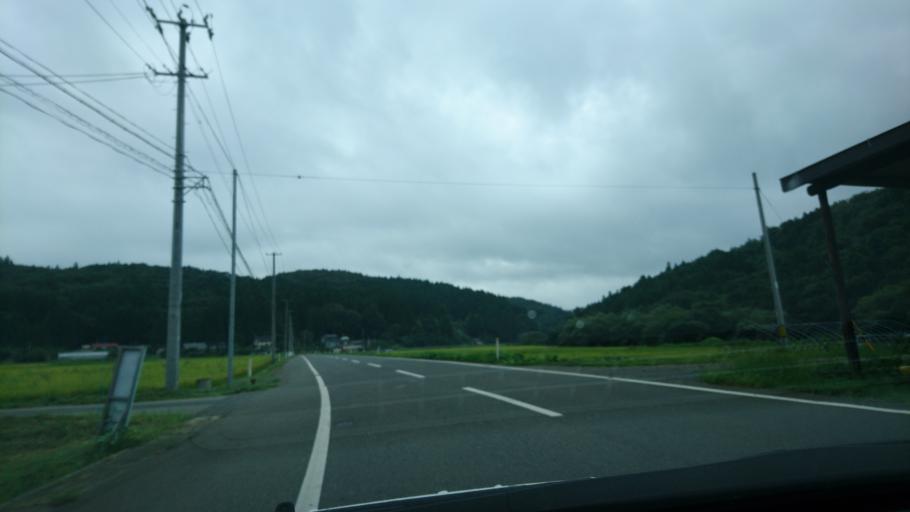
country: JP
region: Iwate
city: Ichinoseki
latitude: 38.9089
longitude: 141.0516
